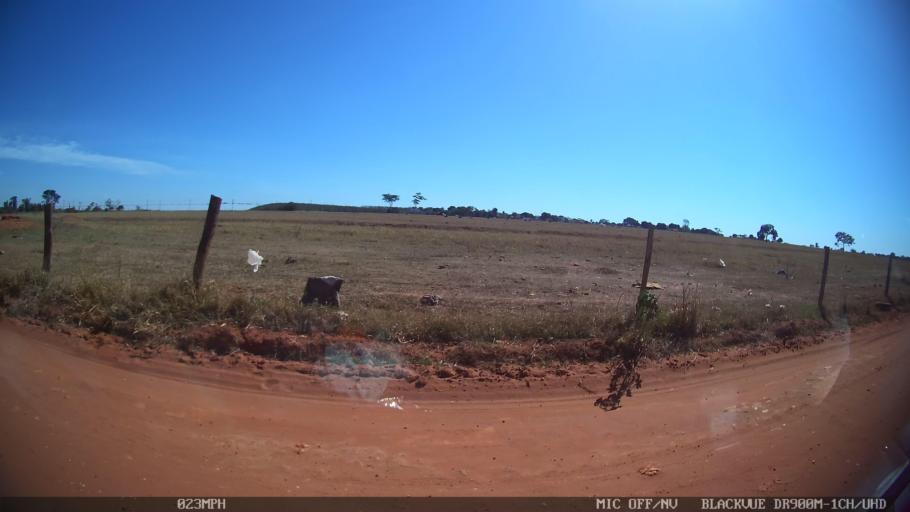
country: BR
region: Sao Paulo
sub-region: Sao Jose Do Rio Preto
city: Sao Jose do Rio Preto
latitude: -20.7433
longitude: -49.4316
